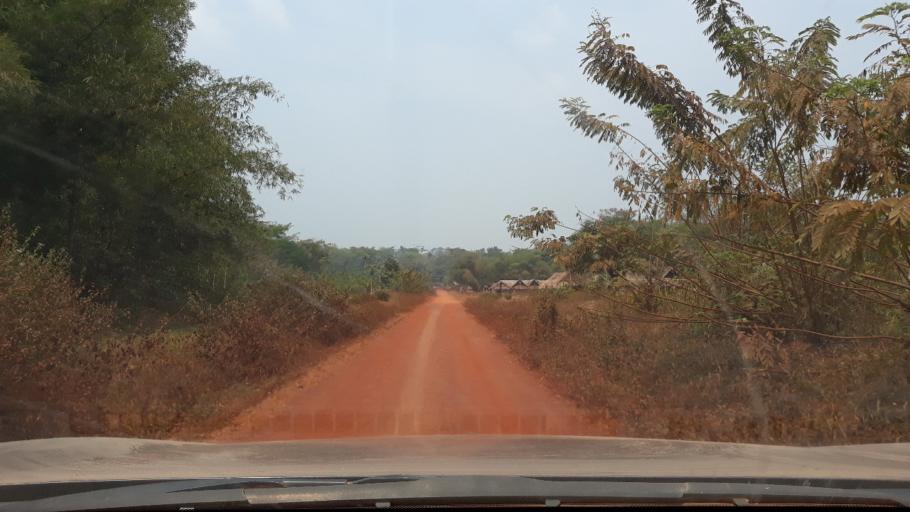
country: CD
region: Eastern Province
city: Buta
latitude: 2.4450
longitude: 24.8735
